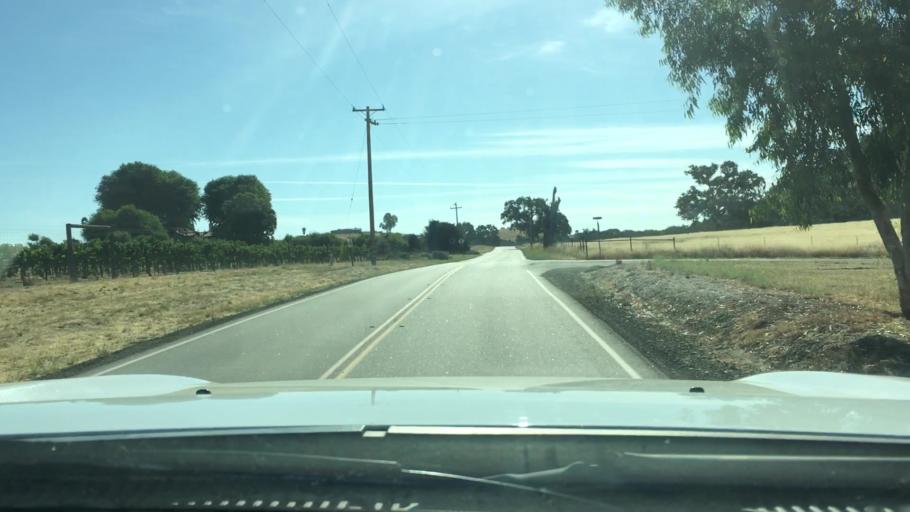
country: US
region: California
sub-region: San Luis Obispo County
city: Templeton
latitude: 35.5626
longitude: -120.6502
